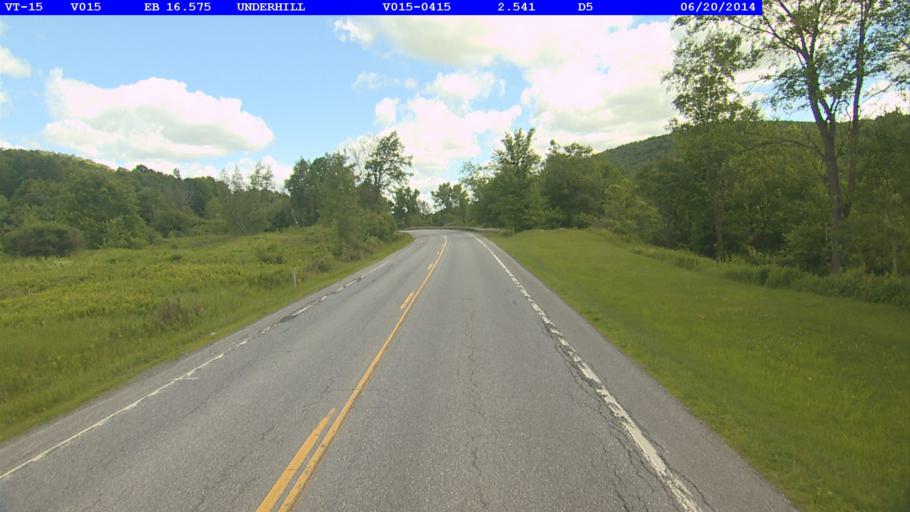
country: US
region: Vermont
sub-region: Chittenden County
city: Jericho
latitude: 44.5604
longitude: -72.9426
